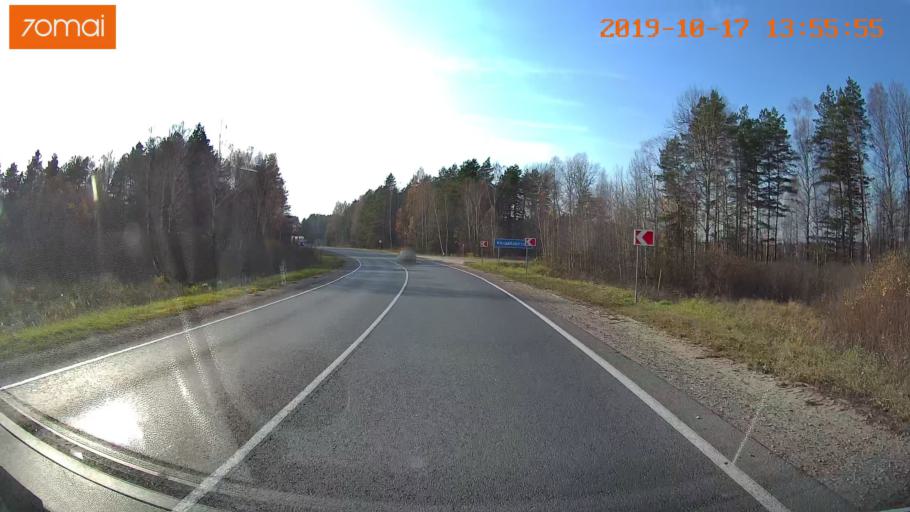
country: RU
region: Rjazan
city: Spas-Klepiki
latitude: 55.1529
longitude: 40.2768
